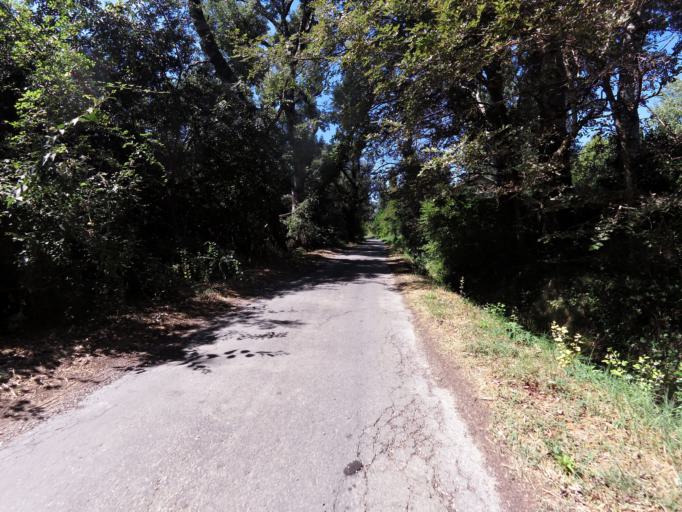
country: FR
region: Languedoc-Roussillon
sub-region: Departement du Gard
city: Aubais
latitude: 43.7570
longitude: 4.1177
